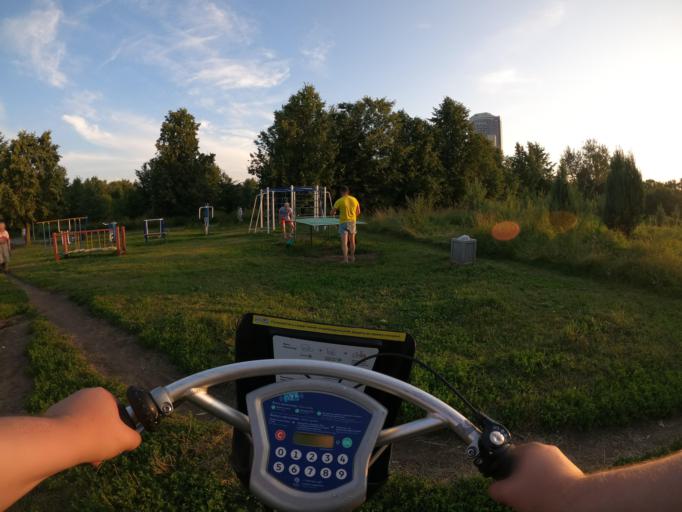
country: RU
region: Moscow
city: Strogino
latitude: 55.8080
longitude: 37.4296
